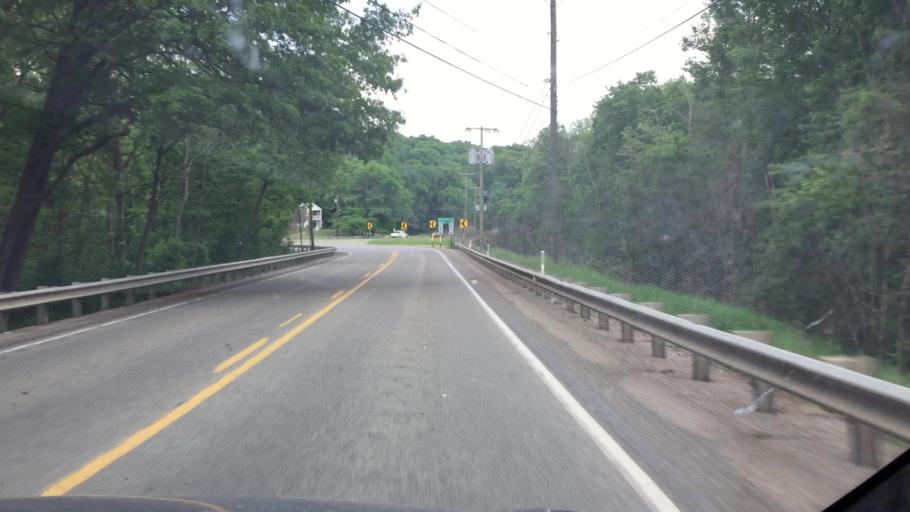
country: US
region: Pennsylvania
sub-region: Butler County
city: Slippery Rock
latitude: 41.0130
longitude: -80.0046
